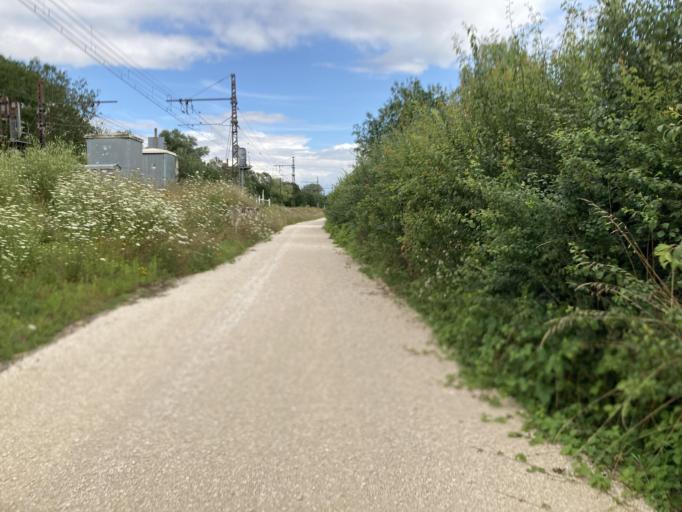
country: FR
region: Bourgogne
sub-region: Departement de la Cote-d'Or
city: Montbard
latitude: 47.6145
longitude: 4.3835
